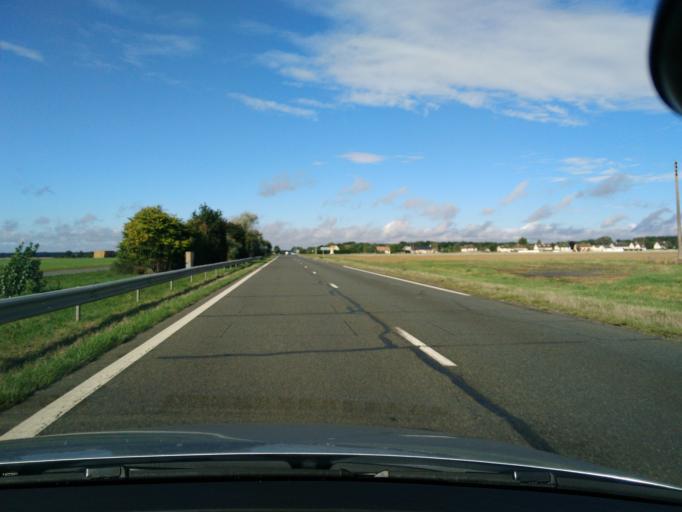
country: FR
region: Centre
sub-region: Departement d'Eure-et-Loir
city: Vert-en-Drouais
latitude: 48.7453
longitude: 1.2833
